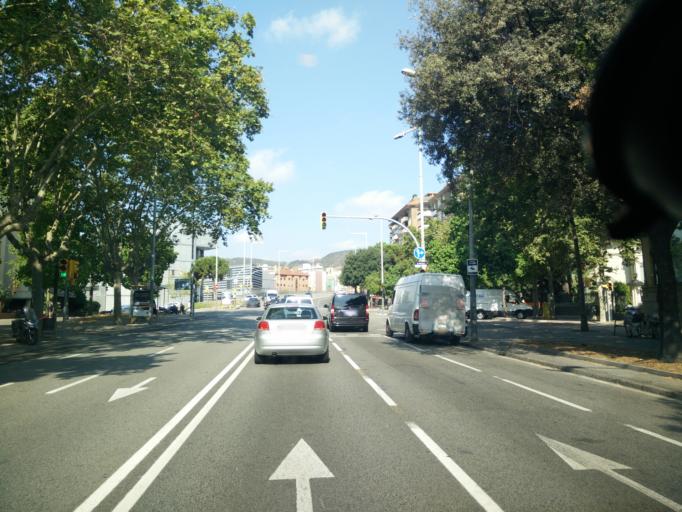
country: ES
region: Catalonia
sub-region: Provincia de Barcelona
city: les Corts
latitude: 41.3978
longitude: 2.1288
